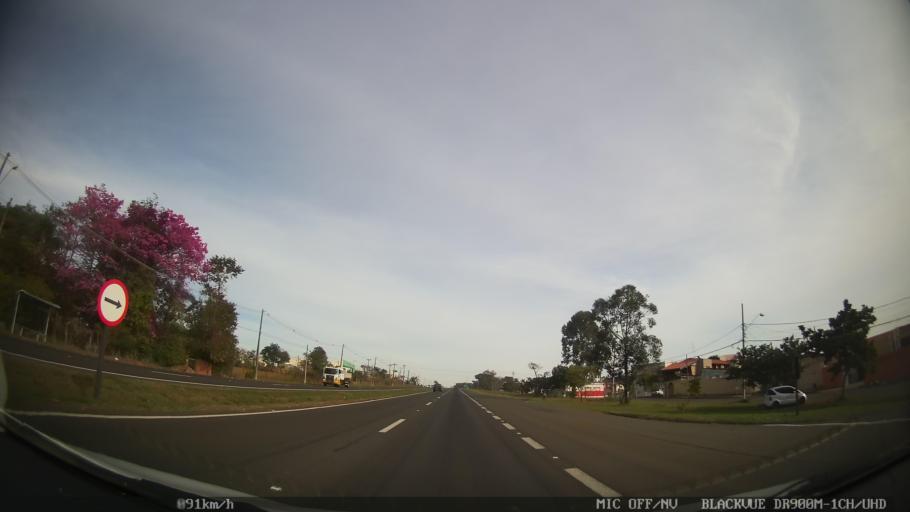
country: BR
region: Sao Paulo
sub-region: Piracicaba
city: Piracicaba
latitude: -22.6816
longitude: -47.6940
